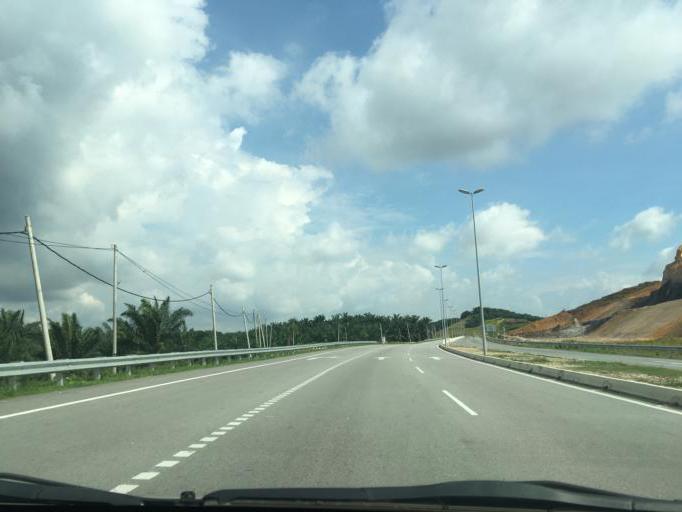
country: MY
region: Selangor
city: Batu Arang
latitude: 3.2953
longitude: 101.4407
